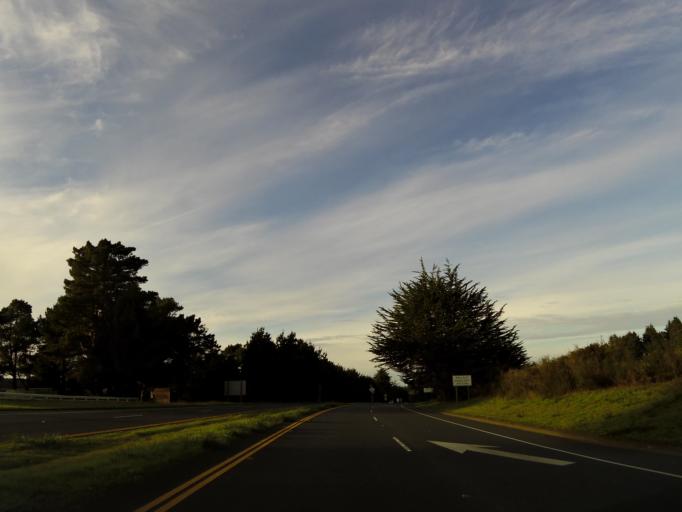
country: US
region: California
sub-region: Mendocino County
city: Fort Bragg
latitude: 39.3103
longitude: -123.7966
